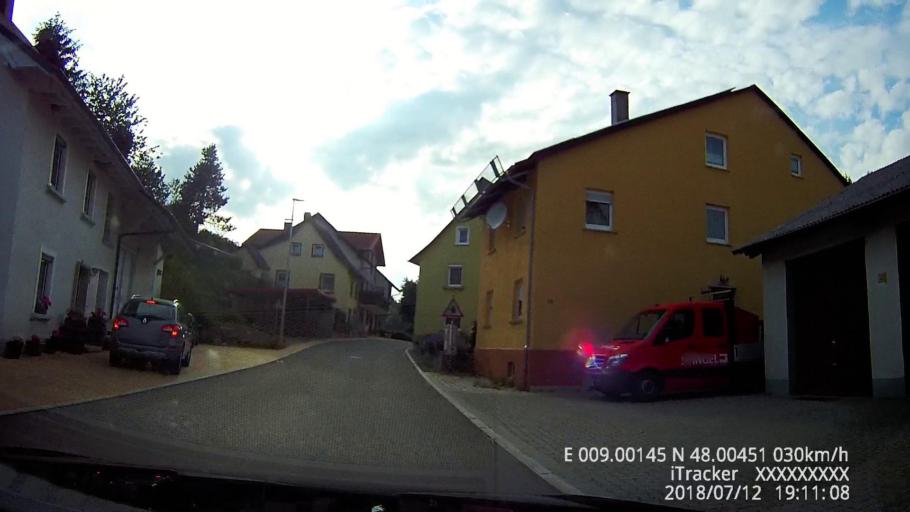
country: DE
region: Baden-Wuerttemberg
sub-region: Tuebingen Region
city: Leibertingen
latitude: 48.0451
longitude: 9.0144
